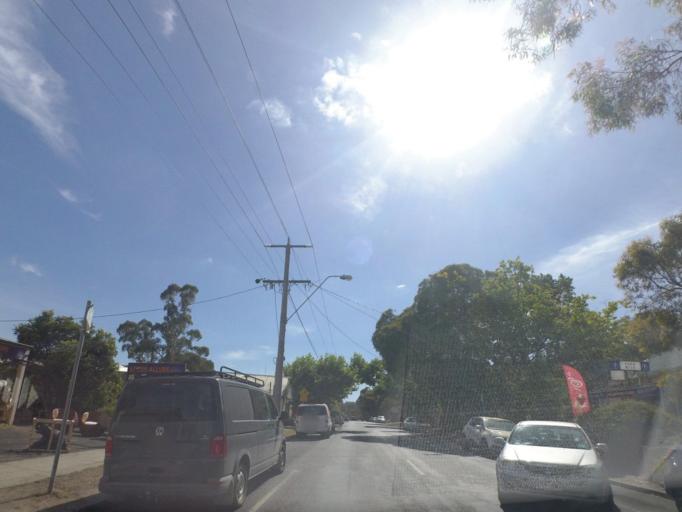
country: AU
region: Victoria
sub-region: Nillumbik
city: Hurstbridge
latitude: -37.6370
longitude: 145.1958
